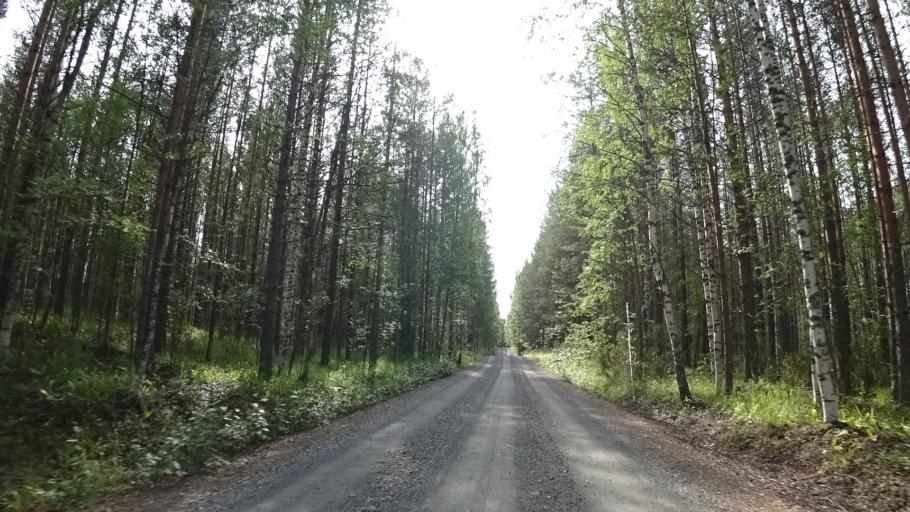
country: FI
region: North Karelia
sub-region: Joensuu
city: Ilomantsi
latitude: 62.6137
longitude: 31.1952
